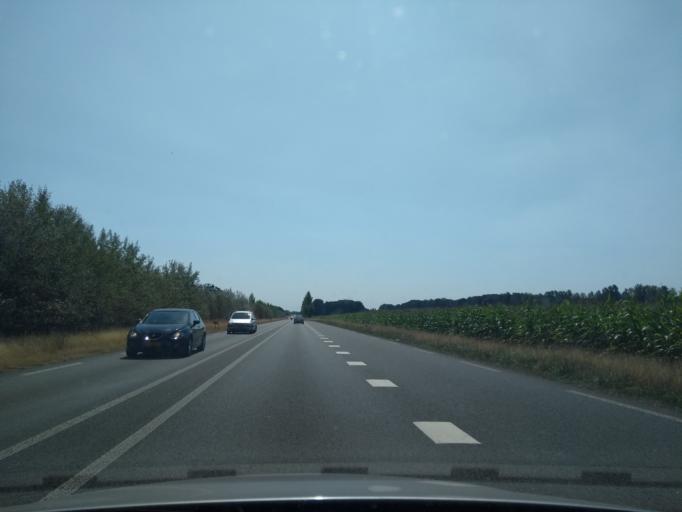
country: NL
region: Overijssel
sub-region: Gemeente Wierden
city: Wierden
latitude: 52.3036
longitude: 6.5524
